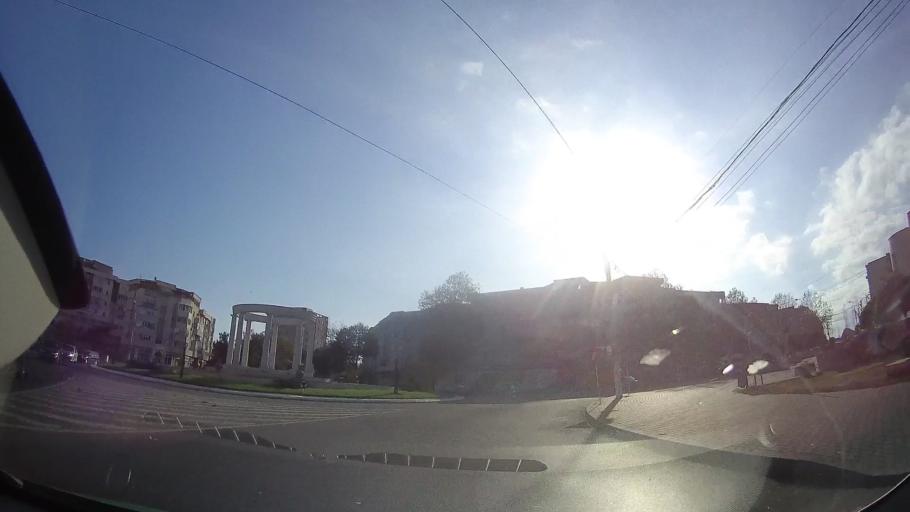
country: RO
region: Constanta
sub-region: Municipiul Mangalia
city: Mangalia
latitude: 43.8175
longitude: 28.5831
